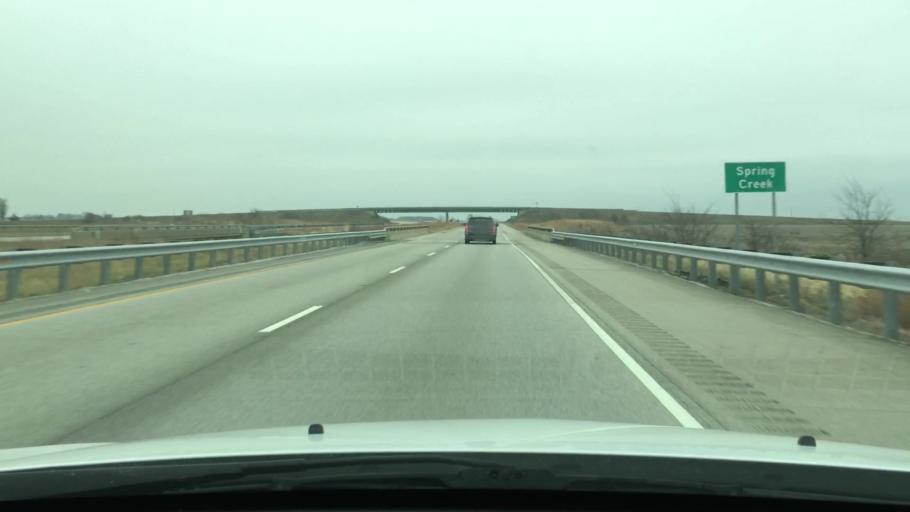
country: US
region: Illinois
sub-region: Sangamon County
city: New Berlin
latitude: 39.7368
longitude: -89.9897
